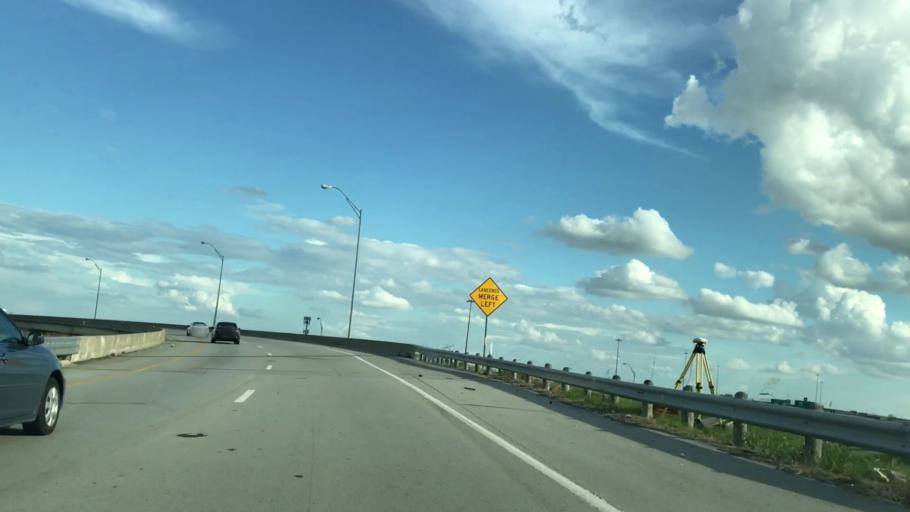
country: US
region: Texas
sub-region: Dallas County
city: Coppell
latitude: 32.9508
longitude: -97.0410
